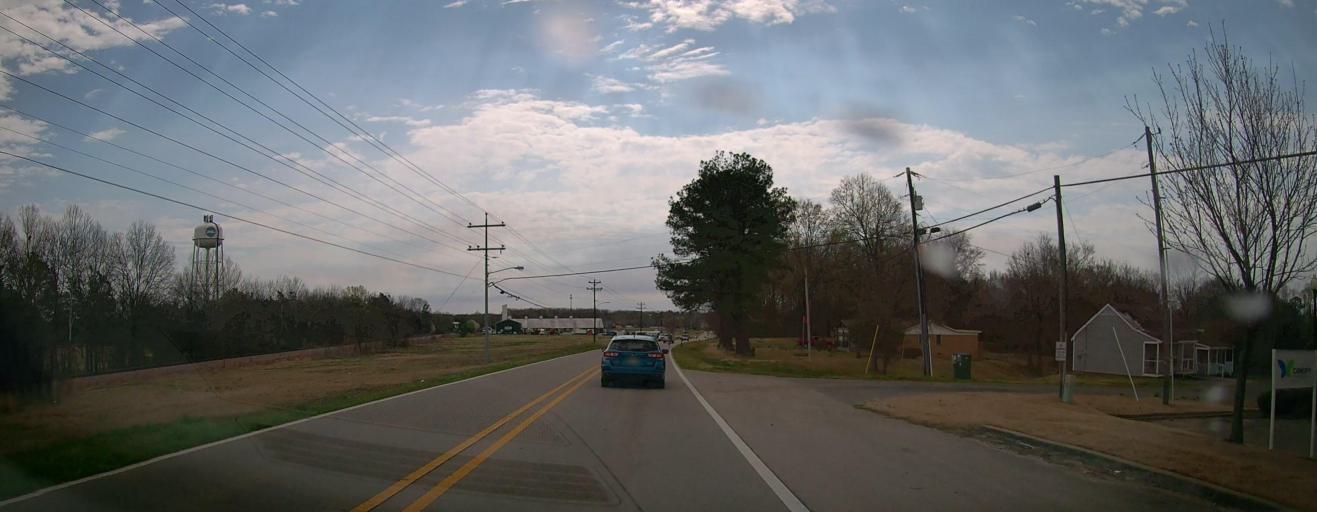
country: US
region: Mississippi
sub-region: De Soto County
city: Olive Branch
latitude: 34.9545
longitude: -89.8156
